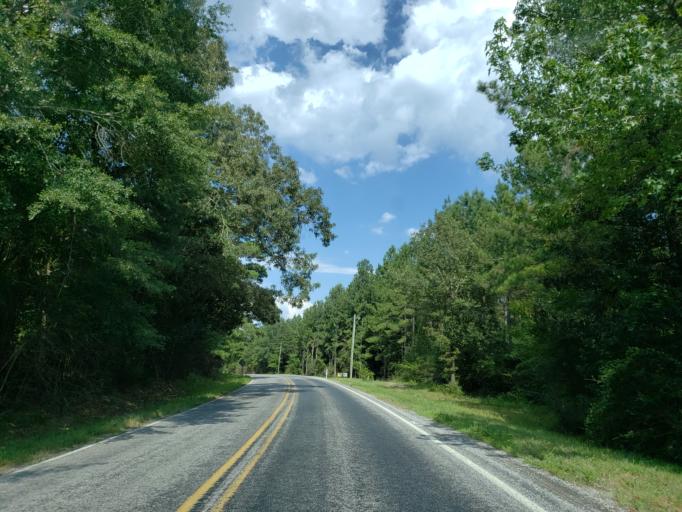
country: US
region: Mississippi
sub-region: Covington County
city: Collins
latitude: 31.6189
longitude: -89.3875
